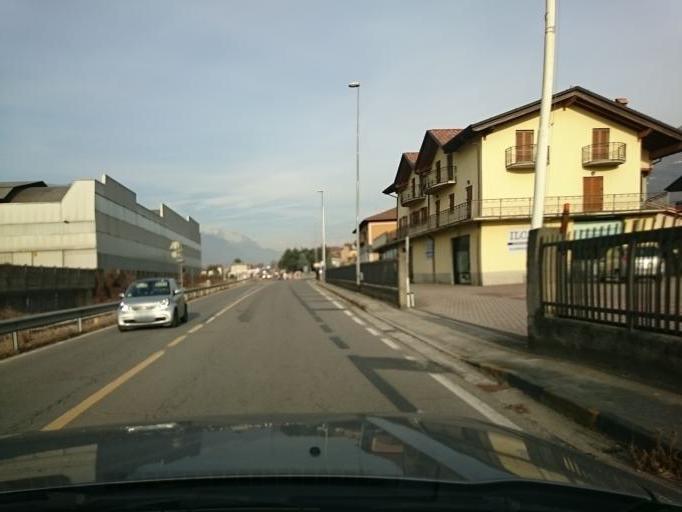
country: IT
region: Lombardy
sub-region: Provincia di Brescia
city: Pian Camuno
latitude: 45.8430
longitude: 10.1423
